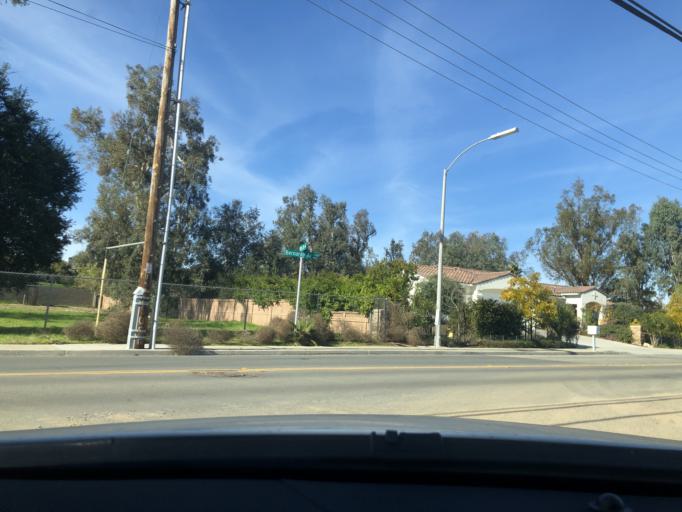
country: US
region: California
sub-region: San Diego County
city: Escondido
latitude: 33.0887
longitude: -117.0897
